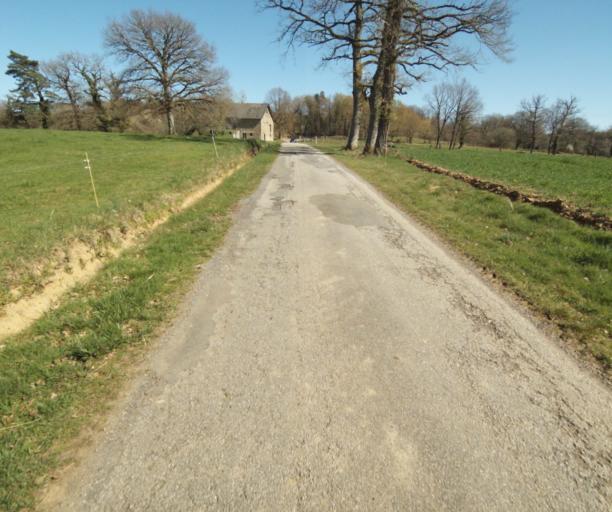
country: FR
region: Limousin
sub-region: Departement de la Correze
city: Chamboulive
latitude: 45.4082
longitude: 1.6535
